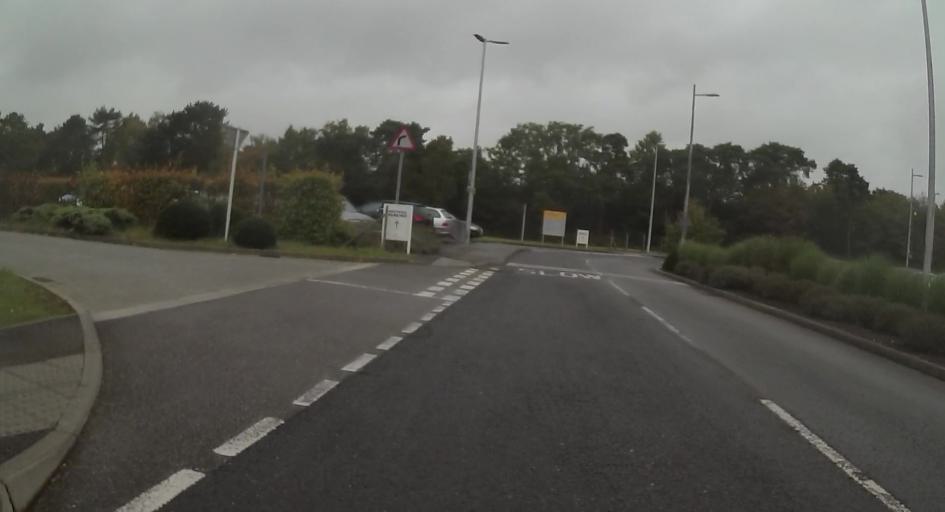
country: GB
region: England
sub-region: Surrey
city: Byfleet
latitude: 51.3539
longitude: -0.4700
